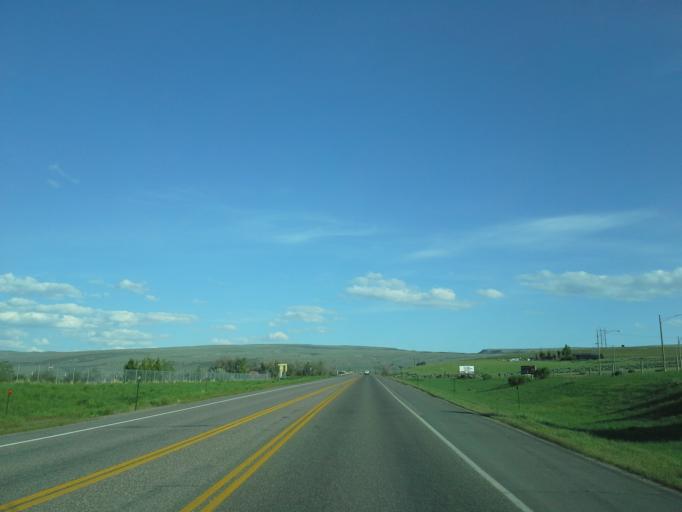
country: US
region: Wyoming
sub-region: Hot Springs County
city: Thermopolis
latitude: 43.6132
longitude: -108.2196
